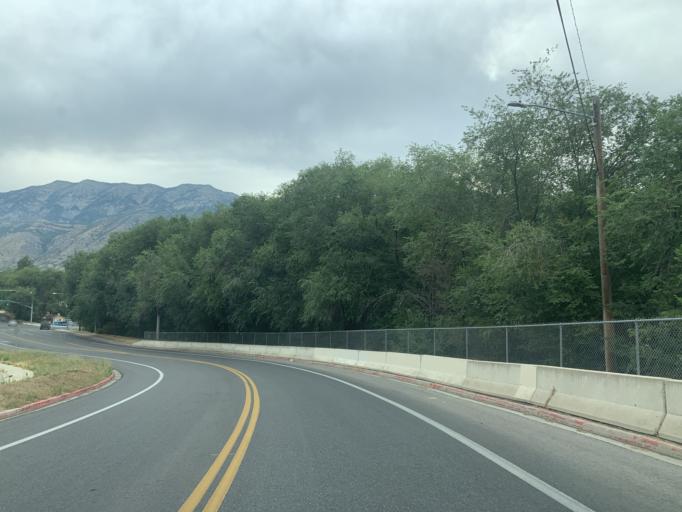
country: US
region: Utah
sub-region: Utah County
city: Provo
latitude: 40.2534
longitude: -111.6755
